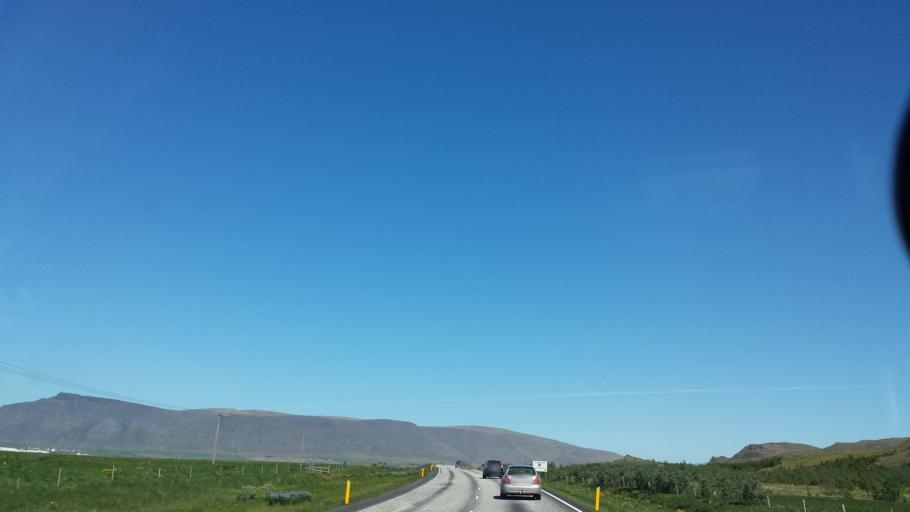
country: IS
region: Capital Region
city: Reykjavik
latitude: 64.2537
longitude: -21.8301
